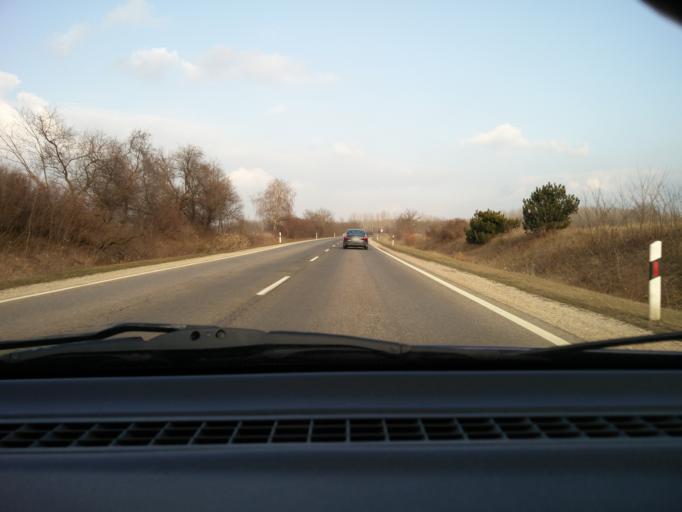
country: HU
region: Pest
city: Nyaregyhaza
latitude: 47.2471
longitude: 19.4510
